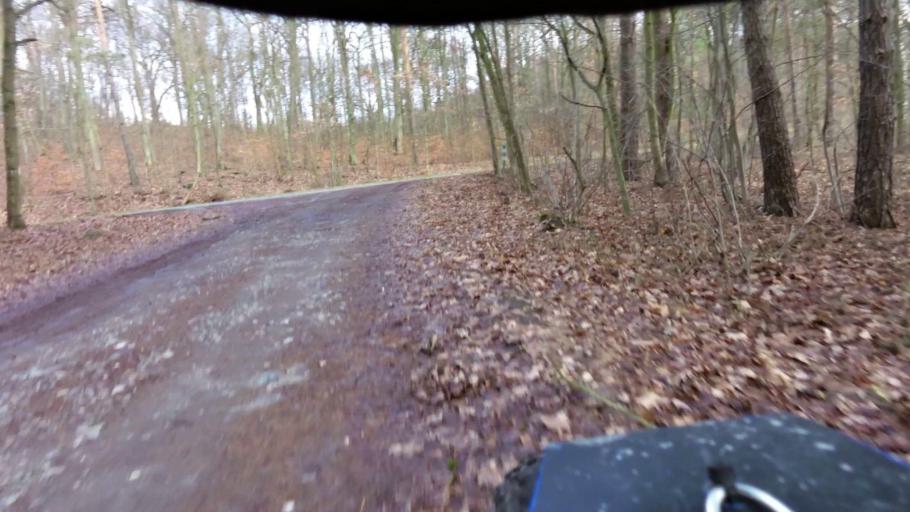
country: PL
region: Lubusz
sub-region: Powiat gorzowski
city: Jenin
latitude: 52.7113
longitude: 15.1146
